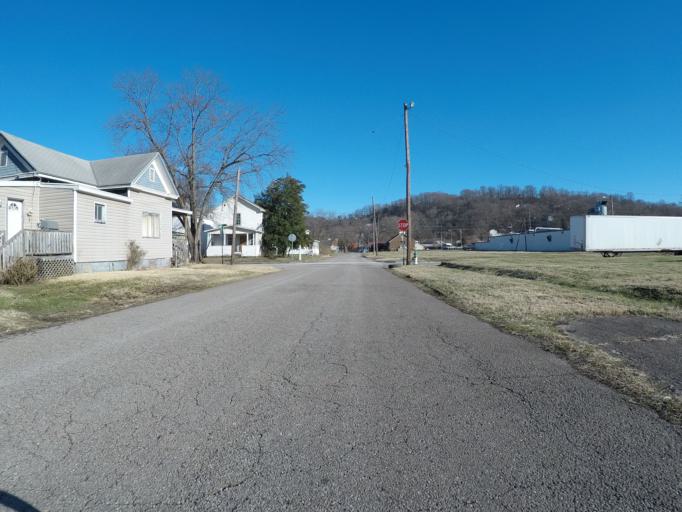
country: US
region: West Virginia
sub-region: Cabell County
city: Huntington
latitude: 38.4266
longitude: -82.3883
